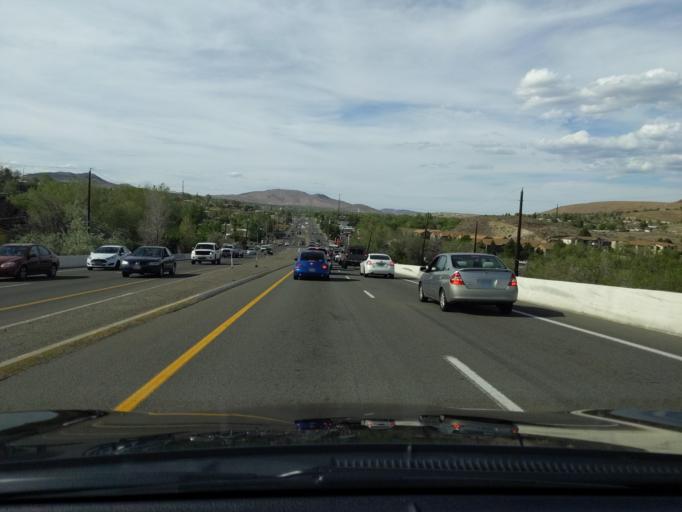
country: US
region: Nevada
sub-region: Washoe County
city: Sun Valley
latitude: 39.5683
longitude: -119.7823
